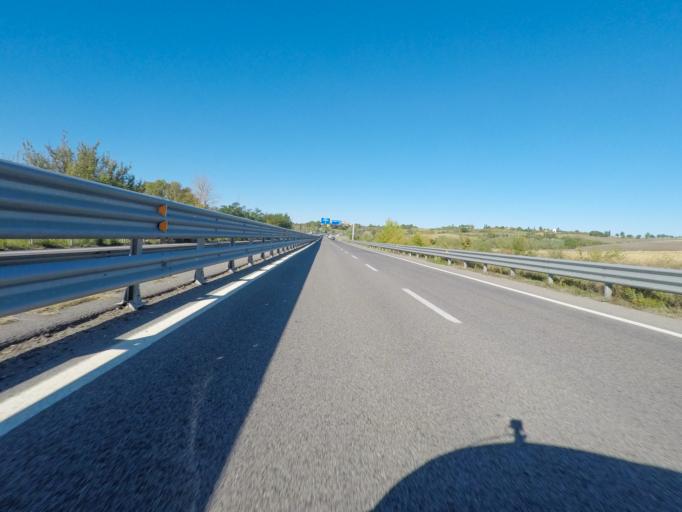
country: IT
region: Tuscany
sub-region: Provincia di Siena
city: Rosia
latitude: 43.2366
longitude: 11.2786
